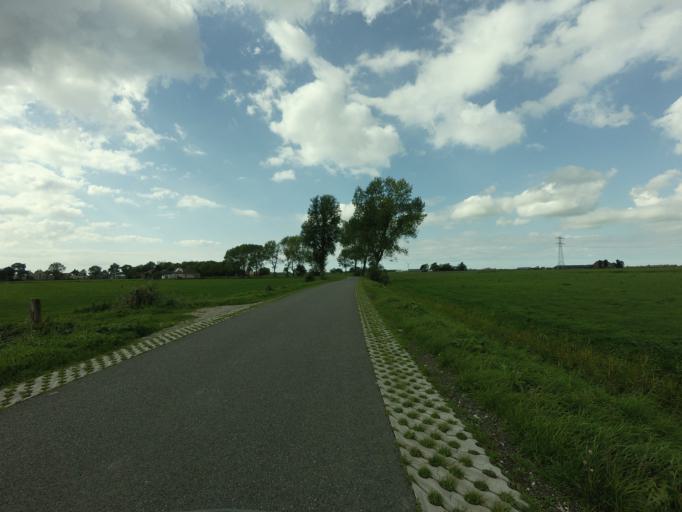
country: NL
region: Friesland
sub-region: Sudwest Fryslan
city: Bolsward
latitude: 53.0677
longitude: 5.5739
